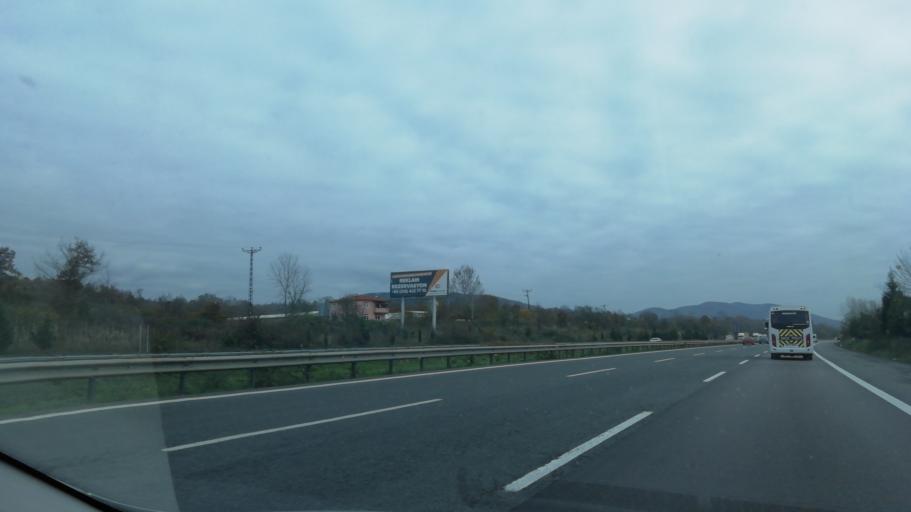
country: TR
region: Sakarya
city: Karadere
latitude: 40.7837
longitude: 30.8079
